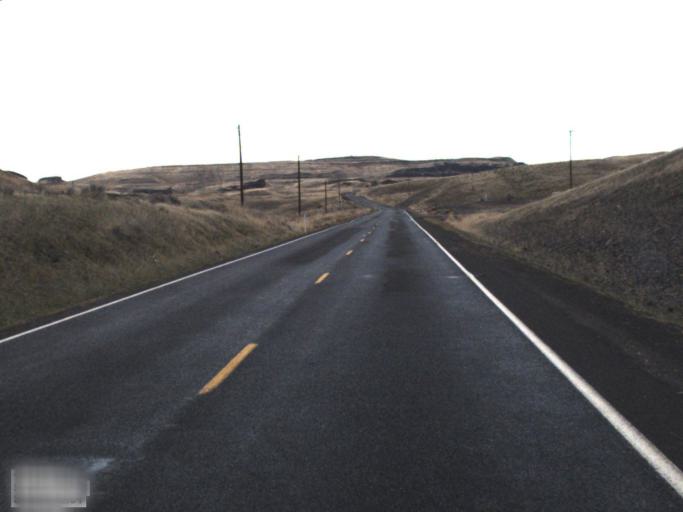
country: US
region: Washington
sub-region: Walla Walla County
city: Waitsburg
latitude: 46.5677
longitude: -118.1924
